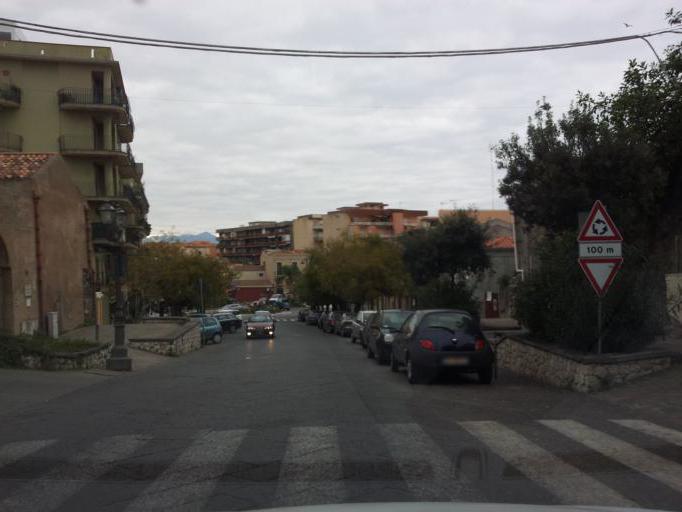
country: IT
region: Sicily
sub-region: Messina
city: Milazzo
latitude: 38.2261
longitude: 15.2411
